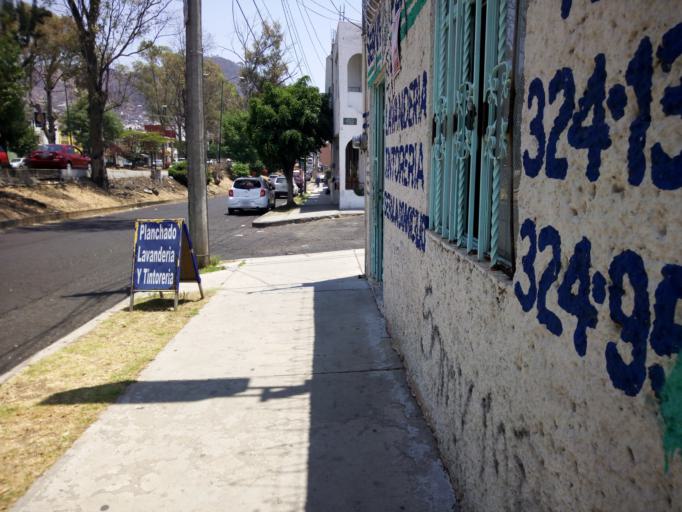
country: MX
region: Michoacan
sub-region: Morelia
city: Puerto de Buenavista (Lazaro Cardenas)
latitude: 19.6950
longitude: -101.1544
